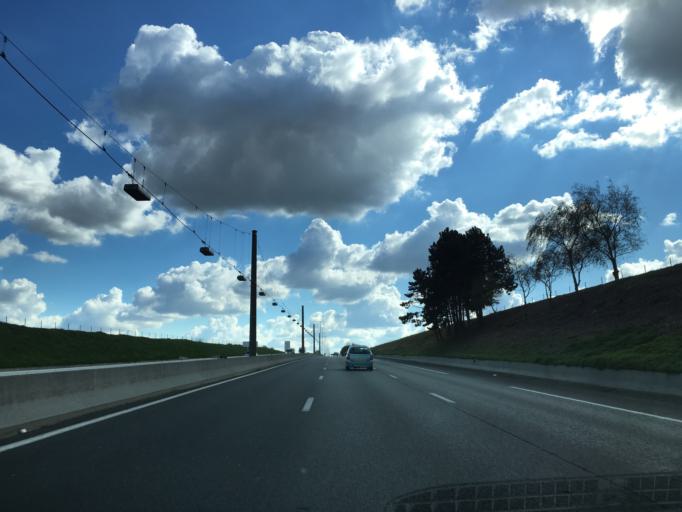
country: FR
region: Nord-Pas-de-Calais
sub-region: Departement du Pas-de-Calais
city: Fampoux
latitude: 50.2865
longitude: 2.8791
